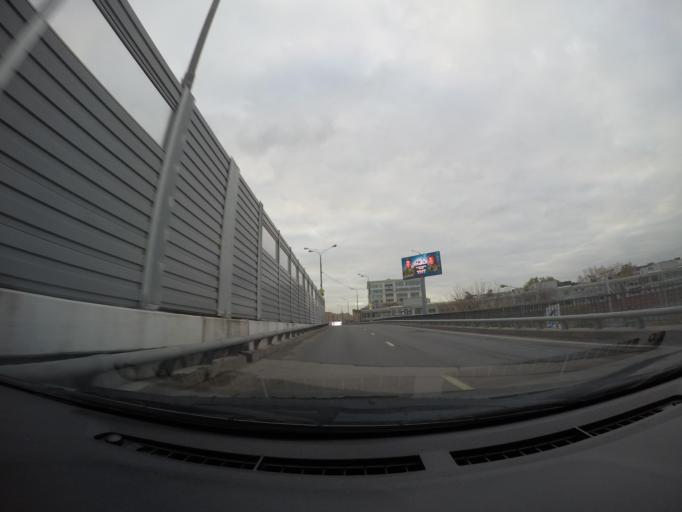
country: RU
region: Moscow
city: Sokol'niki
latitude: 55.7801
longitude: 37.6719
